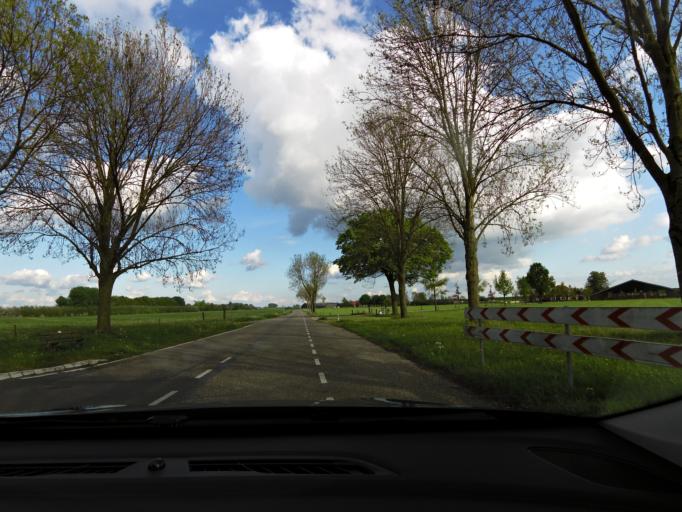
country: NL
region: Gelderland
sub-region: Gemeente Culemborg
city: Culemborg
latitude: 51.9841
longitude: 5.2500
